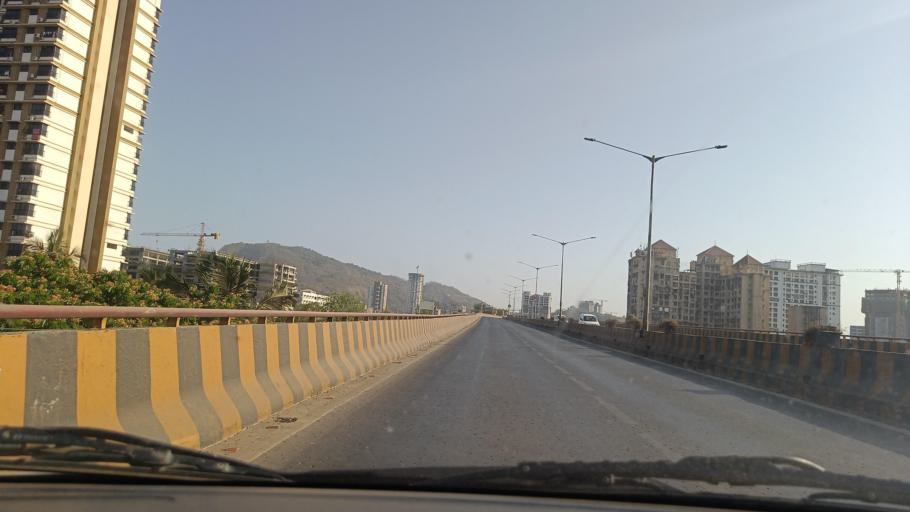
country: IN
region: Maharashtra
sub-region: Mumbai Suburban
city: Mumbai
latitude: 19.0523
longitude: 72.9107
